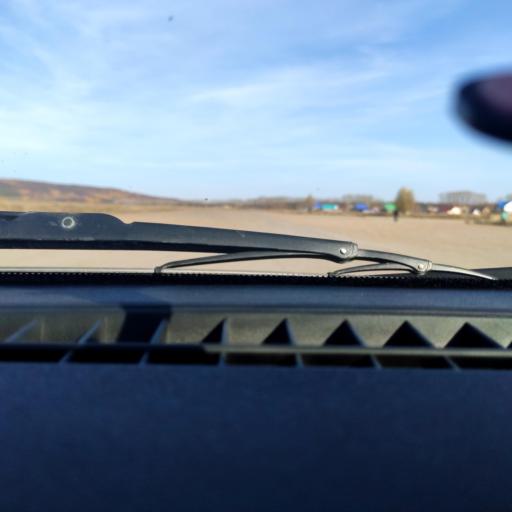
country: RU
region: Bashkortostan
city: Ufa
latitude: 54.8361
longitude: 56.1713
